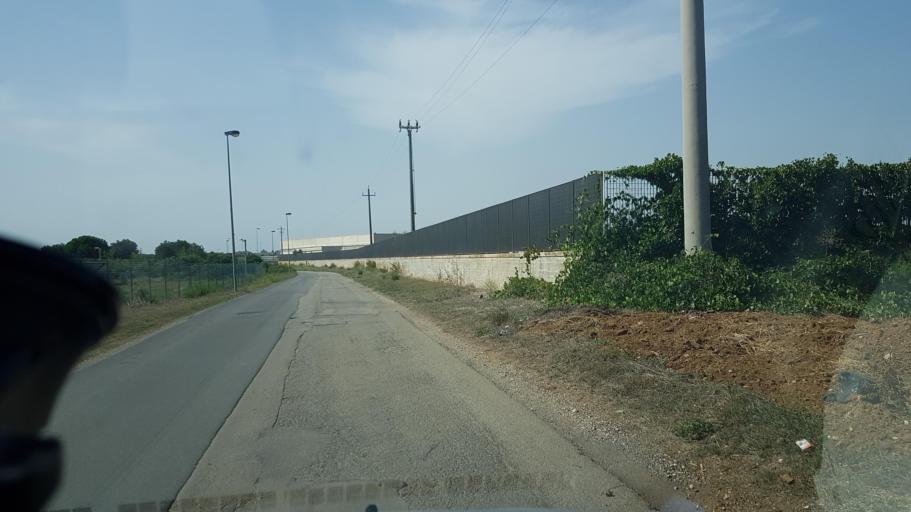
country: IT
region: Apulia
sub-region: Provincia di Brindisi
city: Mesagne
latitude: 40.5687
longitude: 17.8291
